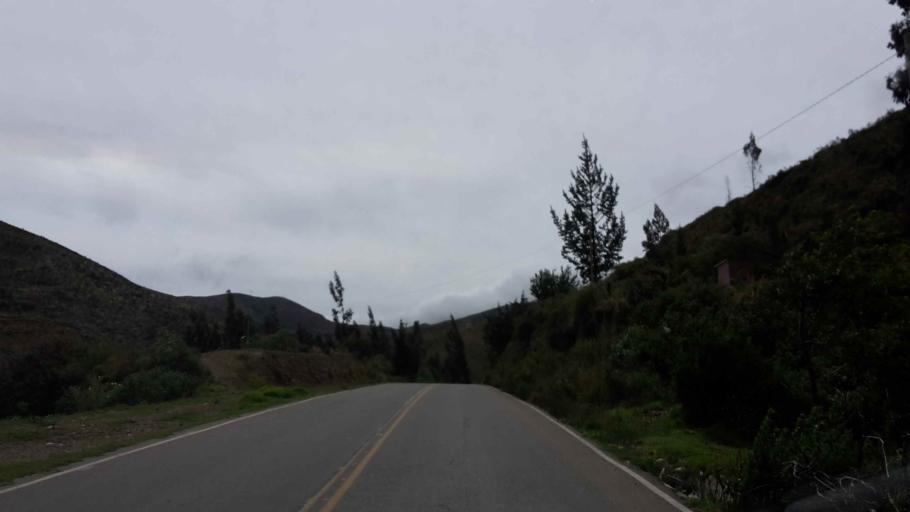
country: BO
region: Cochabamba
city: Colomi
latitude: -17.4014
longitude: -65.7964
